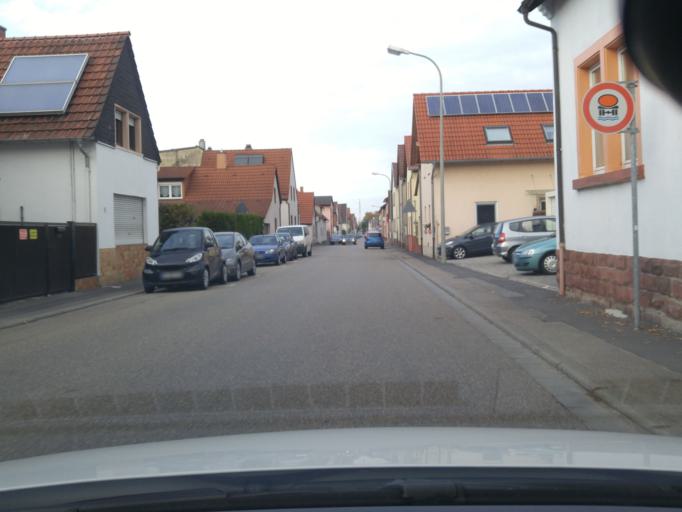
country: DE
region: Rheinland-Pfalz
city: Dudenhofen
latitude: 49.2956
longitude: 8.4074
